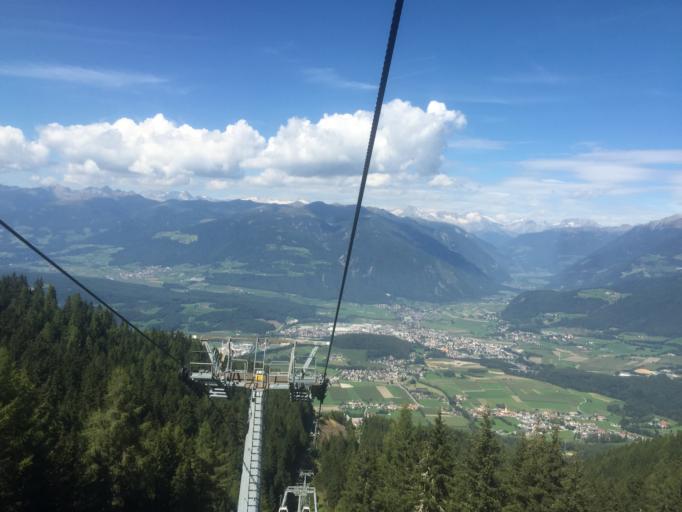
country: IT
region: Trentino-Alto Adige
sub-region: Bolzano
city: Riscone
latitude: 46.7509
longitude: 11.9513
